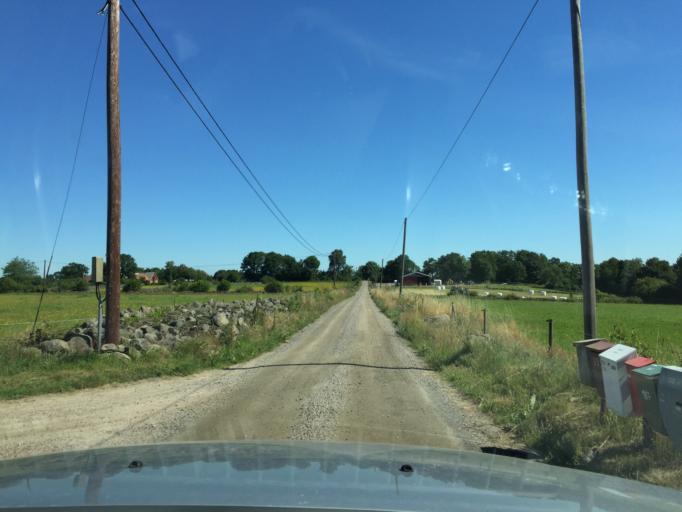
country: SE
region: Skane
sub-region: Hassleholms Kommun
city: Sosdala
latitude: 56.0194
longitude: 13.6406
